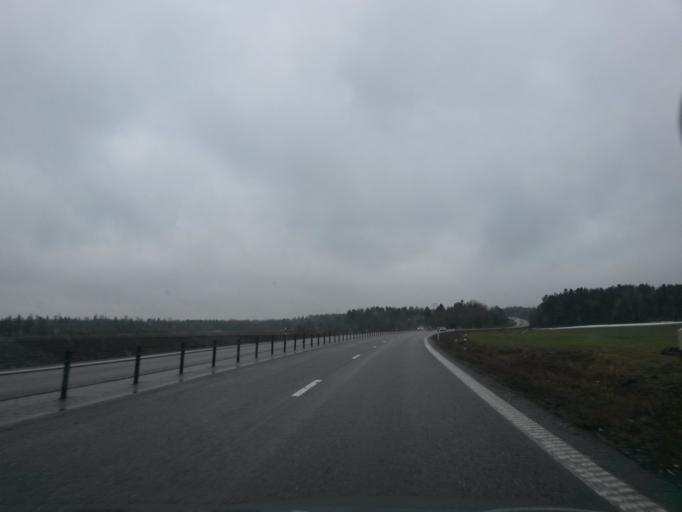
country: SE
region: Vaestra Goetaland
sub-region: Vanersborgs Kommun
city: Vanersborg
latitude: 58.3478
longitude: 12.3128
